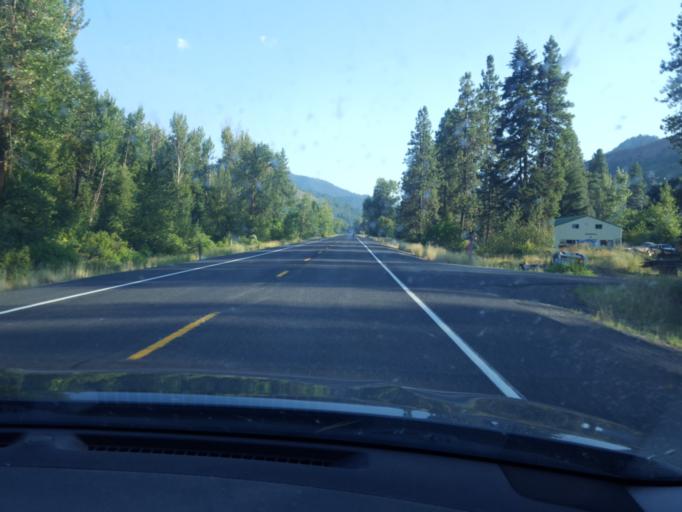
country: US
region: Washington
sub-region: Chelan County
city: Leavenworth
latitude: 47.5308
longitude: -120.6223
